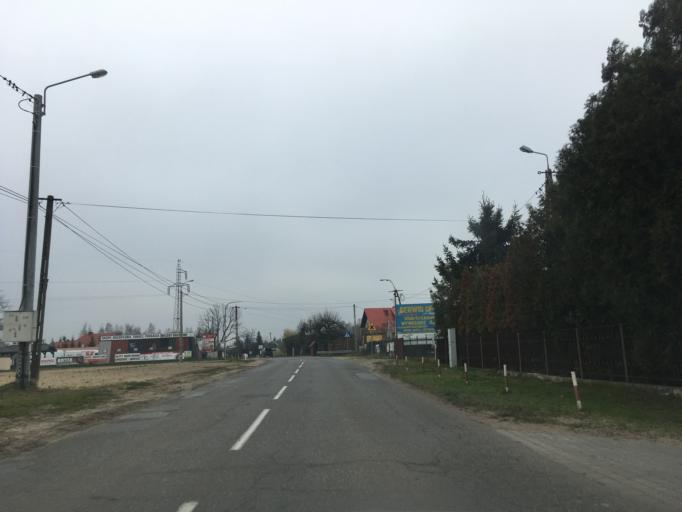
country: PL
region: Masovian Voivodeship
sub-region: Powiat piaseczynski
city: Lesznowola
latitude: 52.0755
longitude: 20.9664
